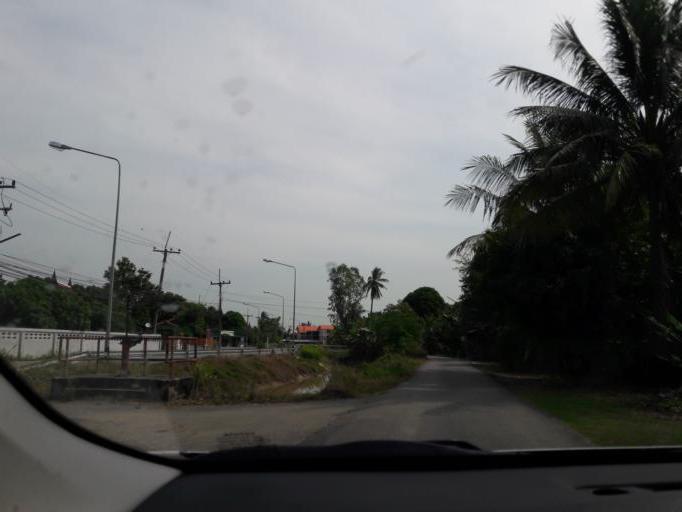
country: TH
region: Ang Thong
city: Ang Thong
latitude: 14.5755
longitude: 100.4721
